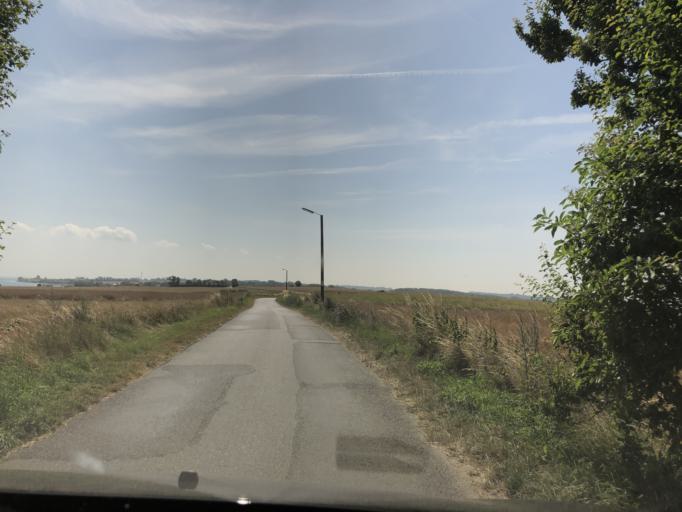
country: DK
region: South Denmark
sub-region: Faaborg-Midtfyn Kommune
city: Faaborg
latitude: 54.9487
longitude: 10.2336
